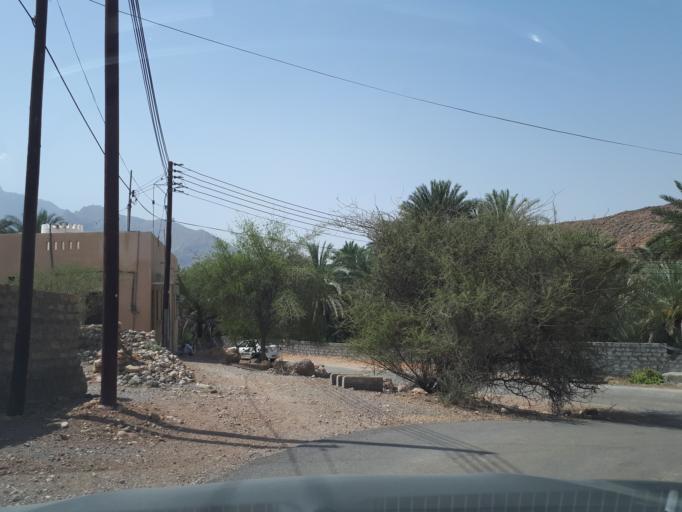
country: OM
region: Ash Sharqiyah
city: Ibra'
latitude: 23.0796
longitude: 58.8716
